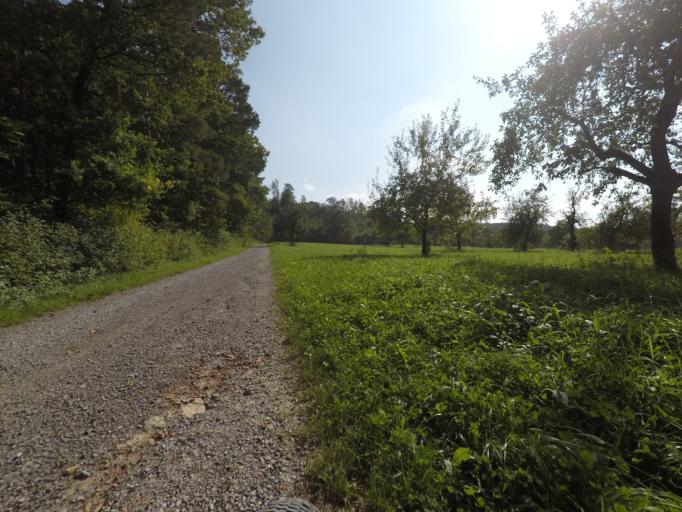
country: DE
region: Baden-Wuerttemberg
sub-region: Regierungsbezirk Stuttgart
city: Weil im Schonbuch
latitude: 48.6406
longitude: 9.0700
